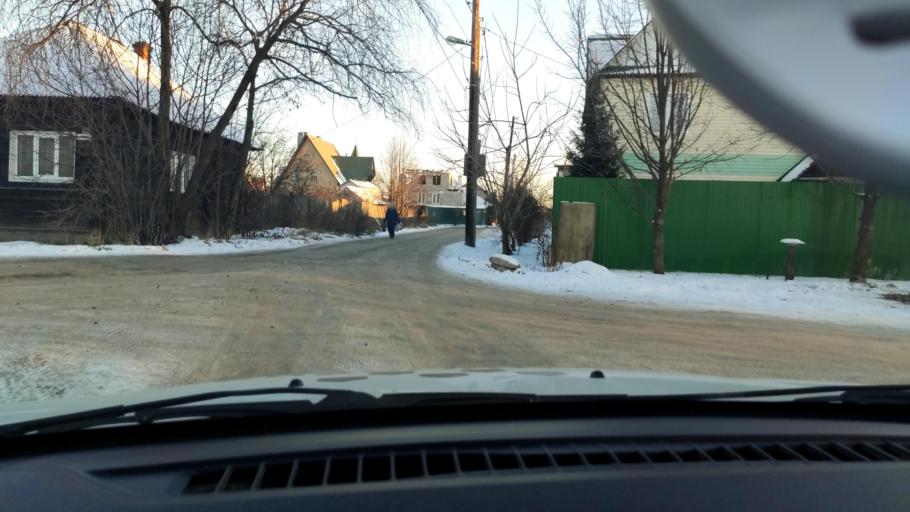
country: RU
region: Perm
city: Perm
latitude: 58.0502
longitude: 56.3320
